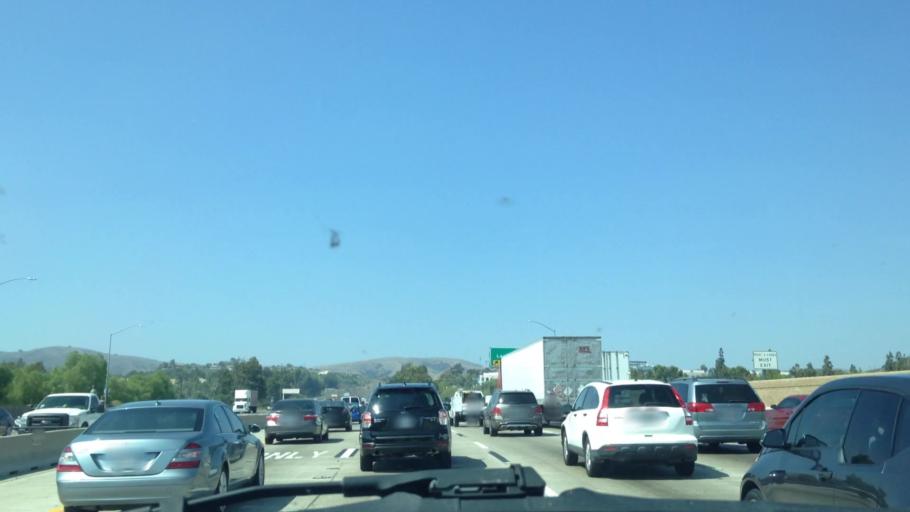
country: US
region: California
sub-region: Orange County
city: Brea
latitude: 33.9210
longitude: -117.8802
